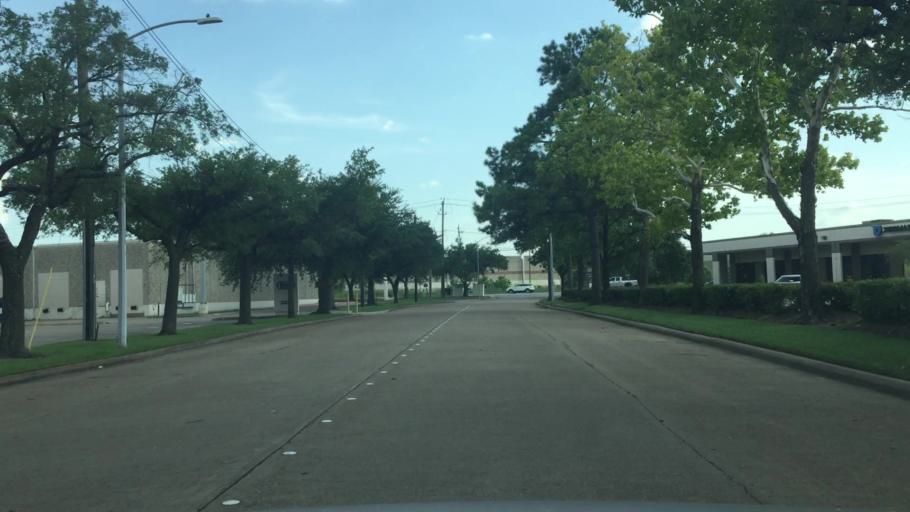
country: US
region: Texas
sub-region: Harris County
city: Spring Valley
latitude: 29.8093
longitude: -95.4687
